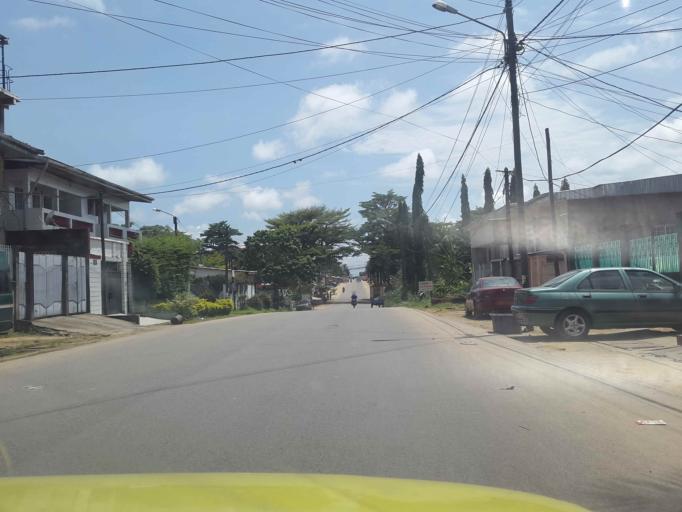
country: CM
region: Littoral
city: Douala
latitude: 4.0884
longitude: 9.7466
